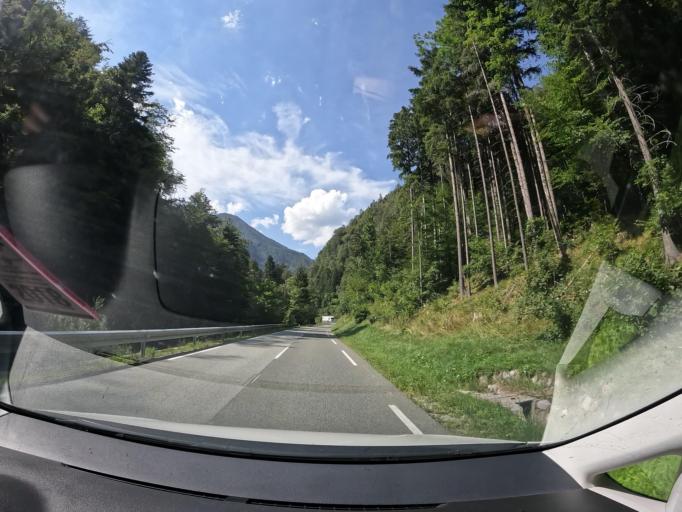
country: SI
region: Jezersko
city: Zgornje Jezersko
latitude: 46.3589
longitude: 14.4616
